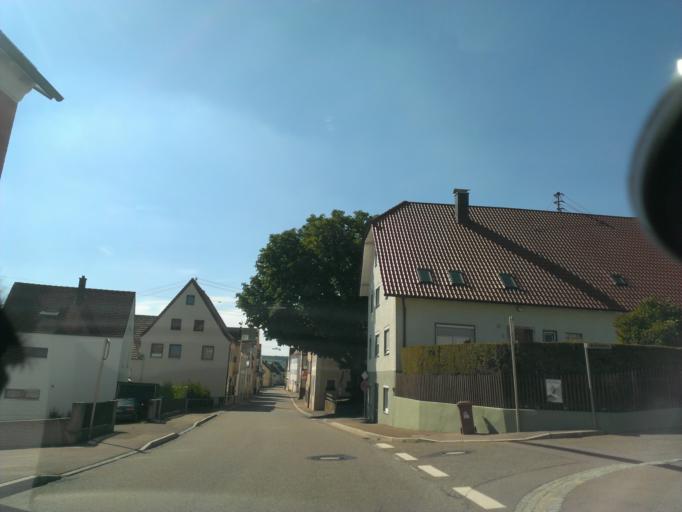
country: DE
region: Bavaria
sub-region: Swabia
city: Bissingen
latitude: 48.7136
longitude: 10.6205
